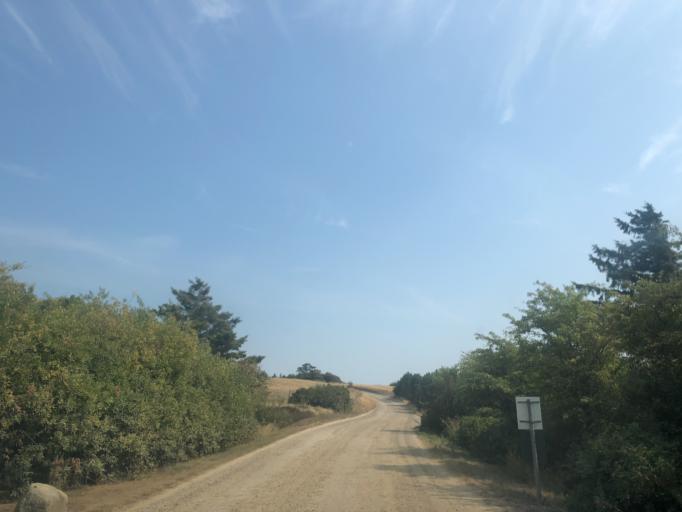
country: DK
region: North Denmark
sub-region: Morso Kommune
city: Nykobing Mors
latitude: 56.8279
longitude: 8.9673
